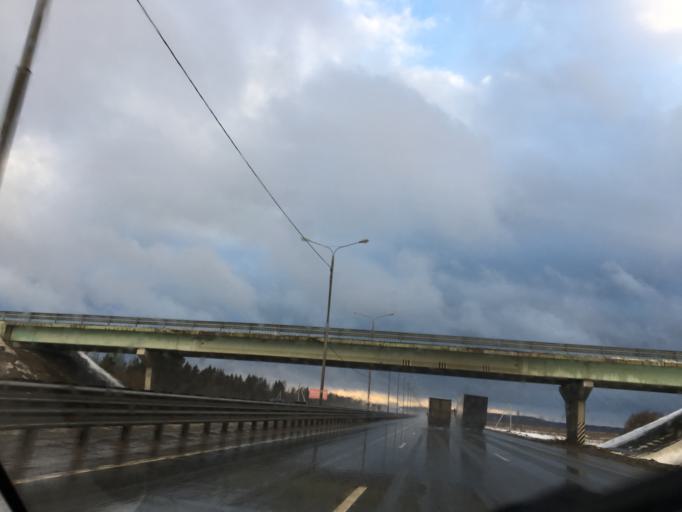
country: RU
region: Moskovskaya
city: Novyy Byt
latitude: 55.0592
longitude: 37.5634
